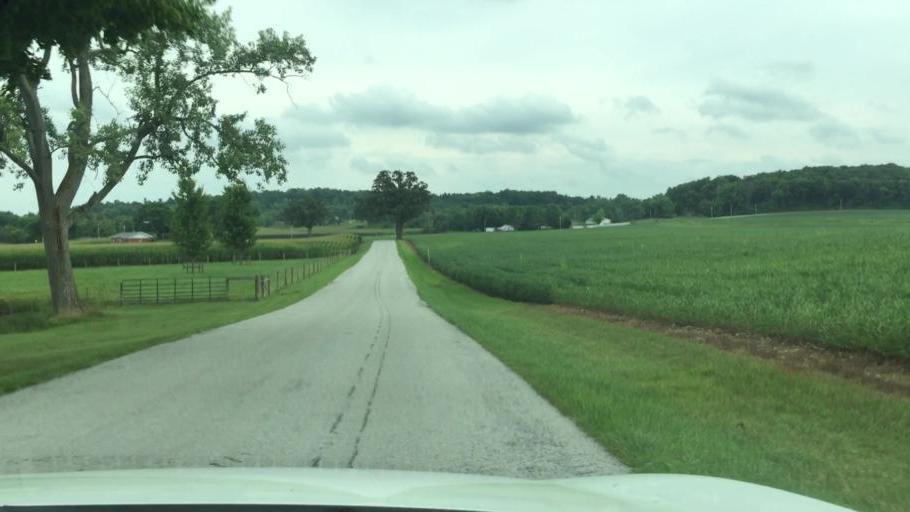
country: US
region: Ohio
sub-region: Clark County
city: Northridge
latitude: 39.9951
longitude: -83.6654
